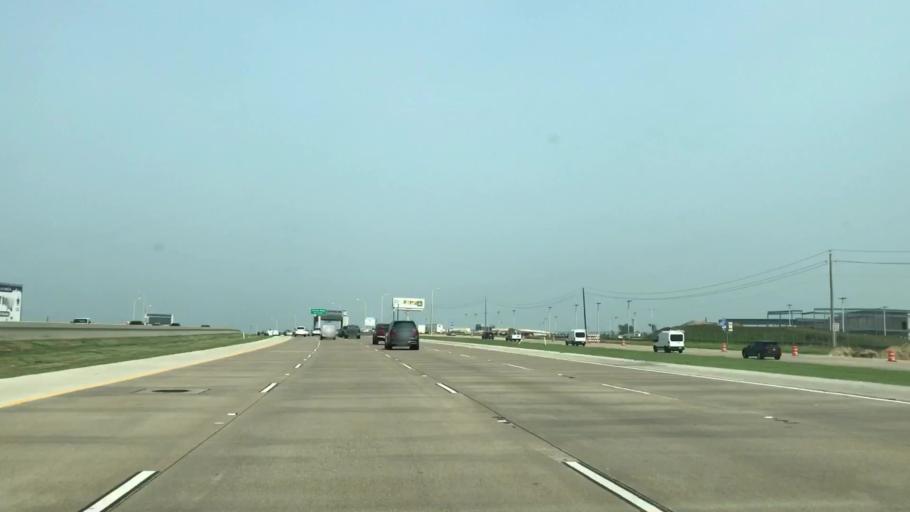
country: US
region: Texas
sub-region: Dallas County
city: Richardson
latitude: 32.9993
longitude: -96.7608
